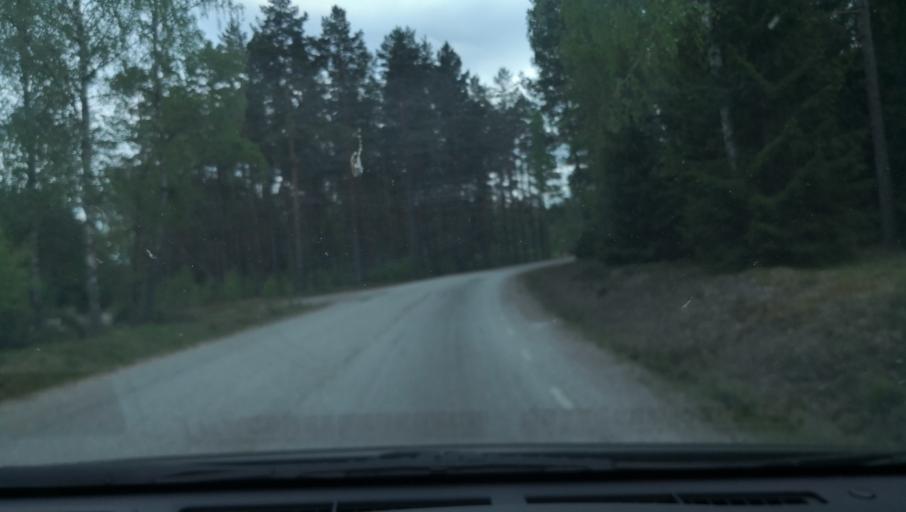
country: SE
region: Vaestmanland
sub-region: Skinnskattebergs Kommun
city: Skinnskatteberg
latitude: 59.8117
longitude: 15.5584
